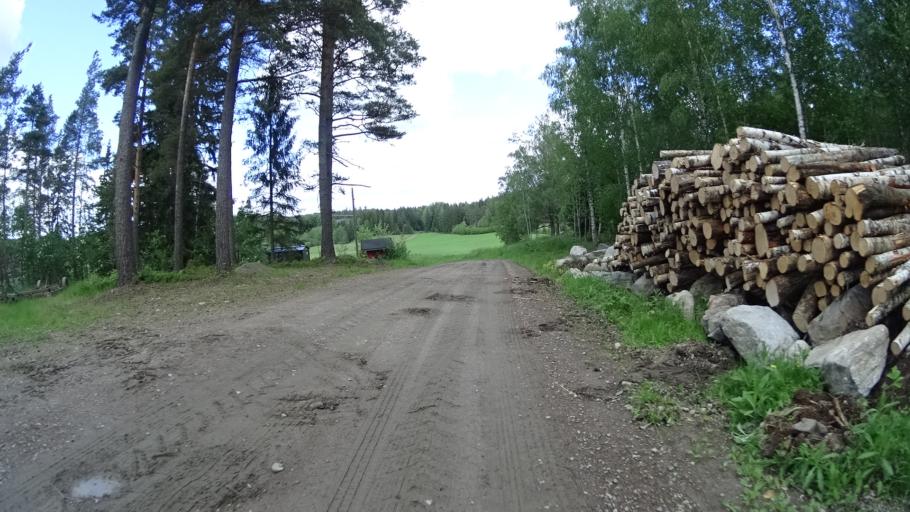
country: FI
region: Uusimaa
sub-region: Raaseporin
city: Karis
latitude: 60.1451
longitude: 23.6201
